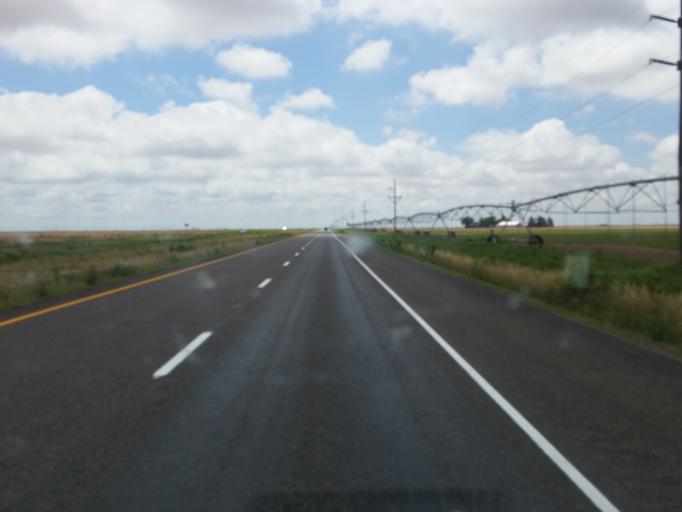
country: US
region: Texas
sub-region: Lubbock County
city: Slaton
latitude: 33.3964
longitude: -101.6077
